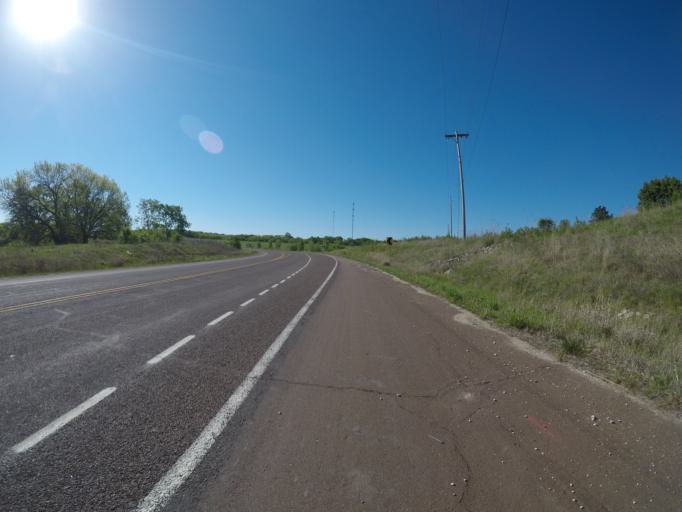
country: US
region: Kansas
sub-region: Douglas County
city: Lawrence
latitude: 39.0028
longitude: -95.3912
